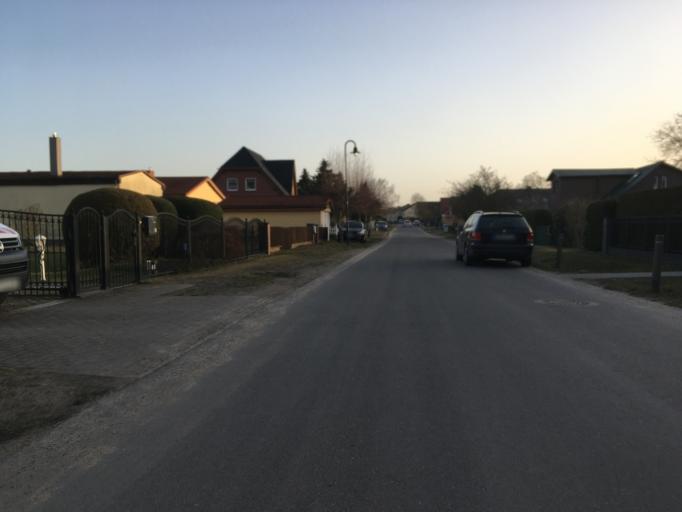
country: DE
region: Berlin
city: Buch
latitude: 52.6341
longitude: 13.5274
